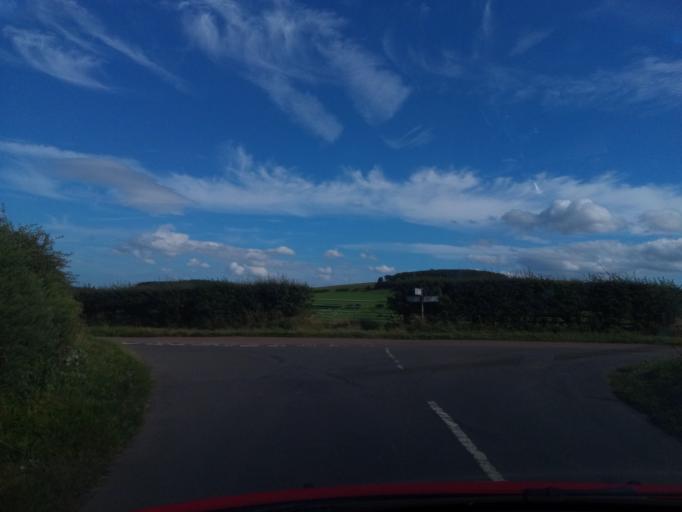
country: GB
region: England
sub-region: Northumberland
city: Kirknewton
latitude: 55.6152
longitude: -2.1697
